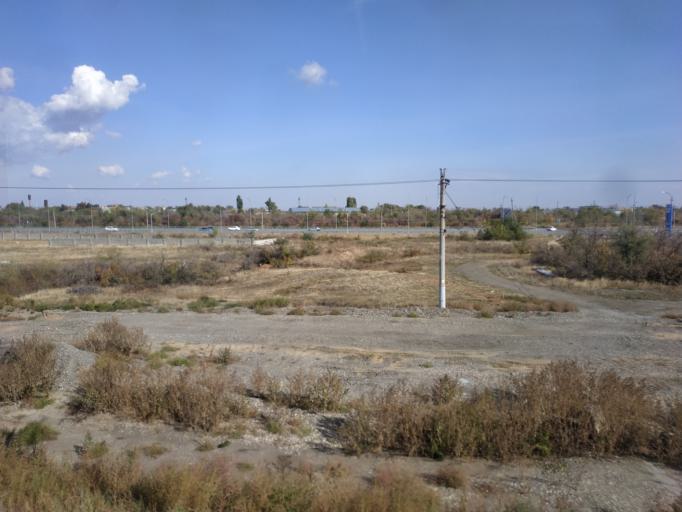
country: RU
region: Volgograd
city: Gumrak
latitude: 48.7703
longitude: 44.3926
